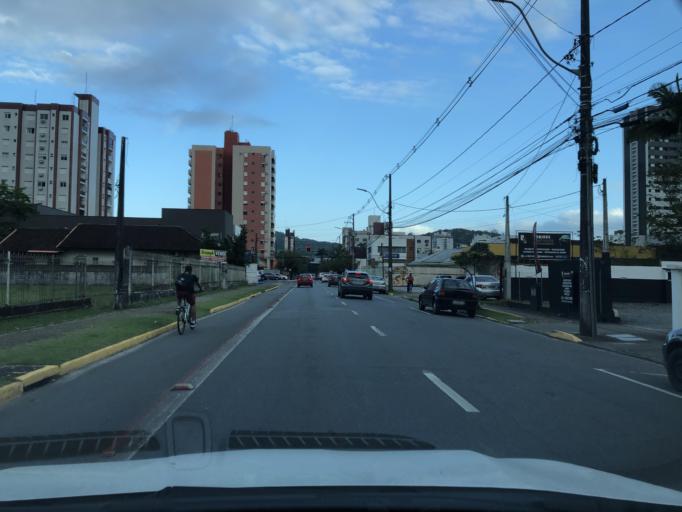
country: BR
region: Santa Catarina
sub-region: Joinville
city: Joinville
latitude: -26.2936
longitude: -48.8513
